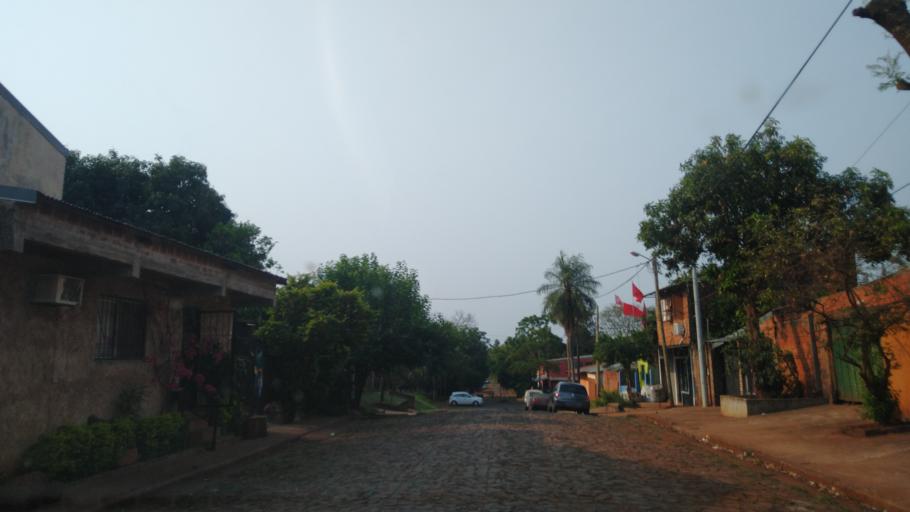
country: AR
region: Misiones
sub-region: Departamento de Capital
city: Posadas
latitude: -27.3850
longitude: -55.9314
